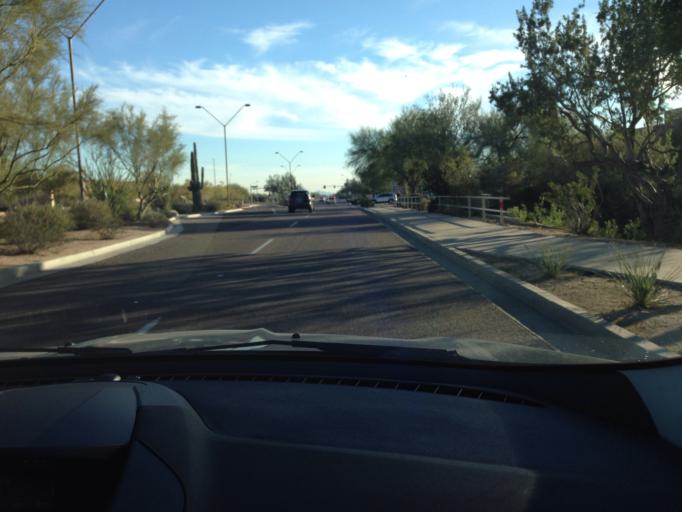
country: US
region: Arizona
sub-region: Maricopa County
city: Cave Creek
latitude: 33.7436
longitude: -111.9783
